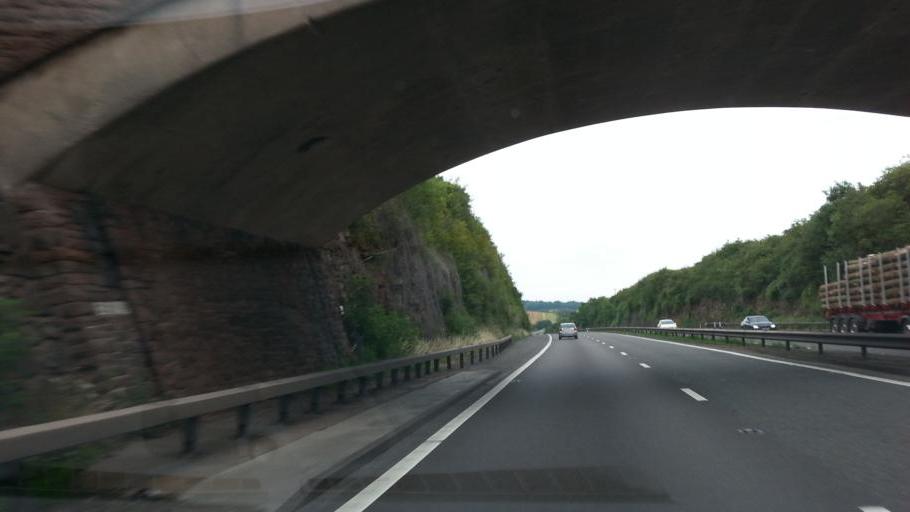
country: GB
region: England
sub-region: Herefordshire
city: Ross on Wye
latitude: 51.9290
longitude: -2.5507
